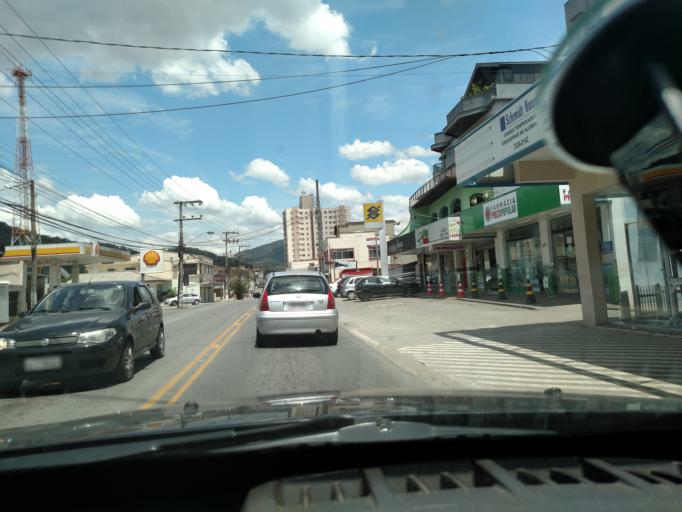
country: BR
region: Santa Catarina
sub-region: Blumenau
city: Blumenau
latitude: -26.9510
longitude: -49.0717
